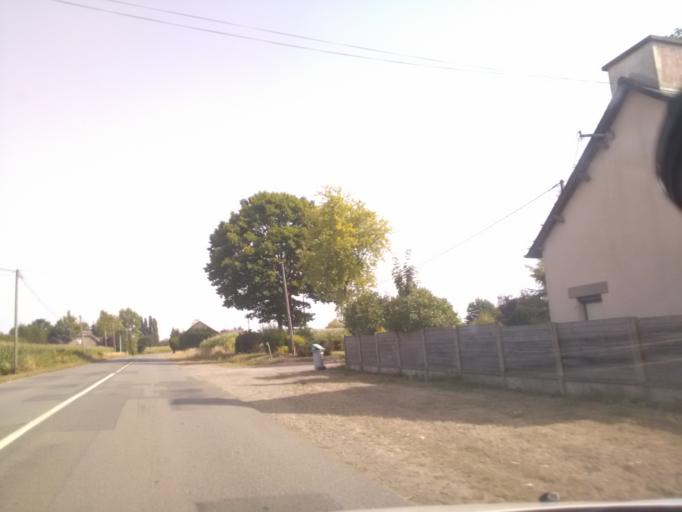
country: FR
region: Brittany
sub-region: Departement d'Ille-et-Vilaine
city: Vignoc
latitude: 48.2499
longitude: -1.7694
